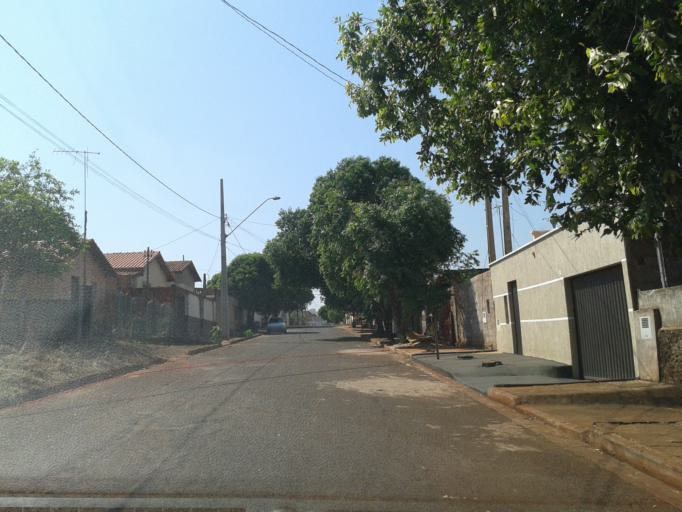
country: BR
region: Minas Gerais
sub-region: Ituiutaba
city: Ituiutaba
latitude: -18.9578
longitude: -49.4525
